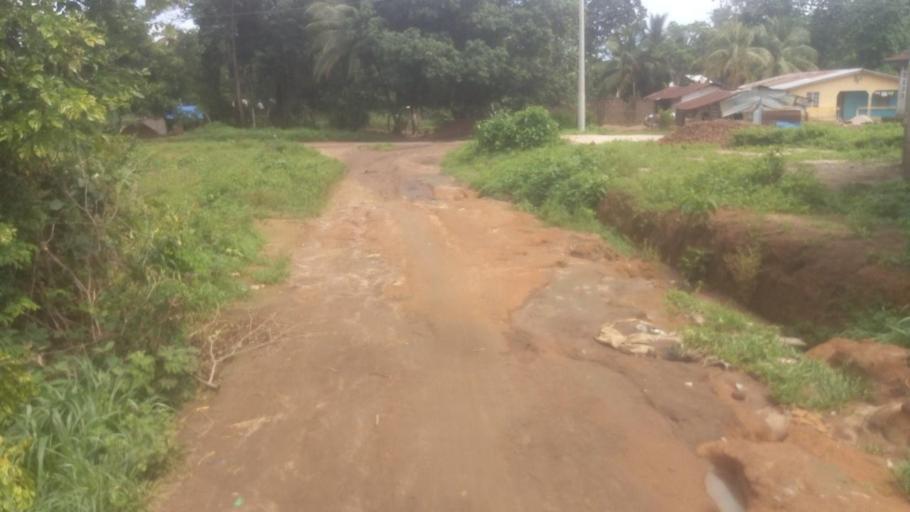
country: SL
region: Northern Province
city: Masoyila
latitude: 8.5948
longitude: -13.1957
